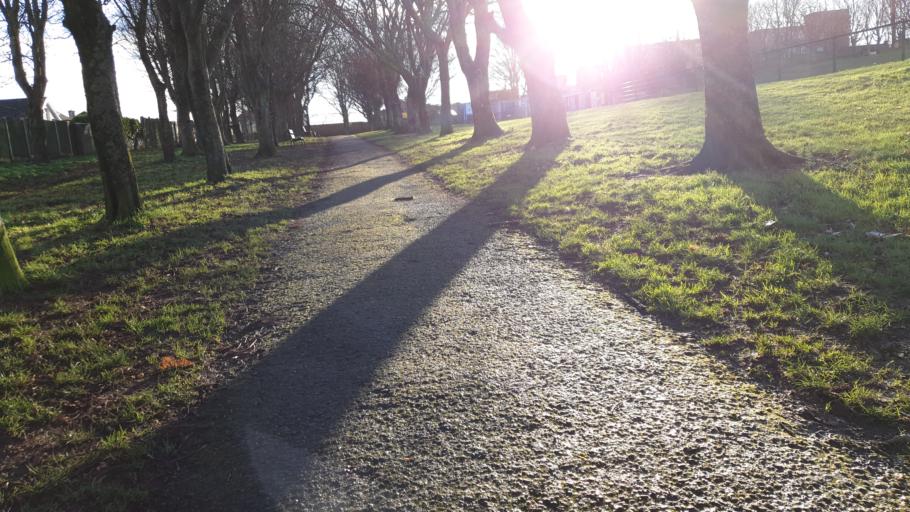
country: IE
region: Munster
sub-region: County Cork
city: Cork
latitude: 51.8907
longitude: -8.4277
